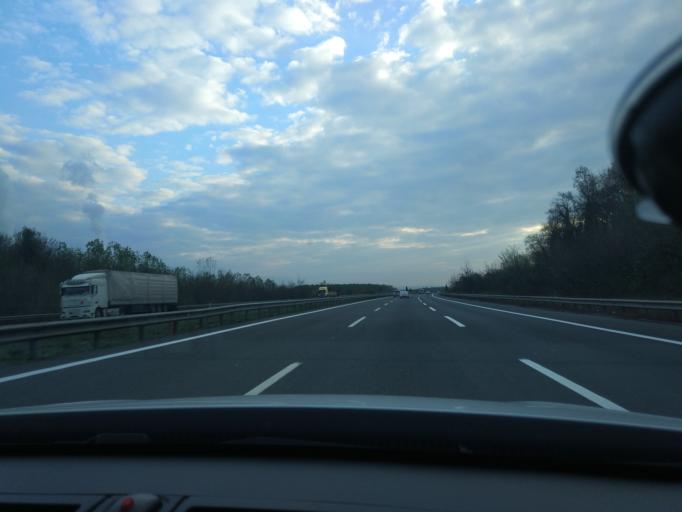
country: TR
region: Sakarya
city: Akyazi
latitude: 40.7390
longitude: 30.6488
